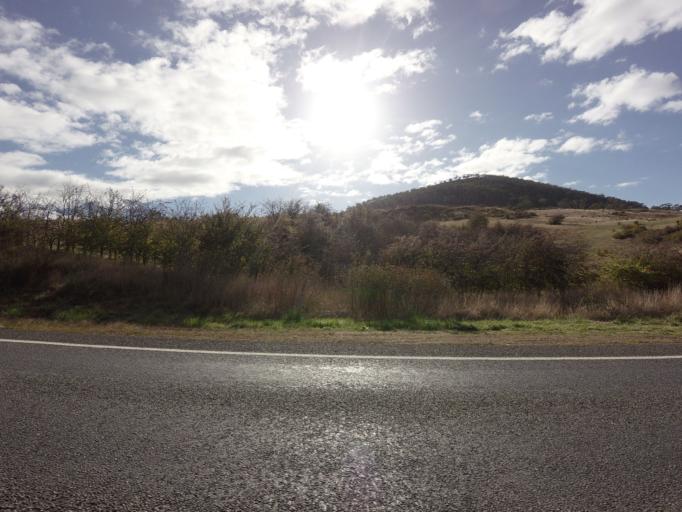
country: AU
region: Tasmania
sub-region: Derwent Valley
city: New Norfolk
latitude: -42.7230
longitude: 146.9505
